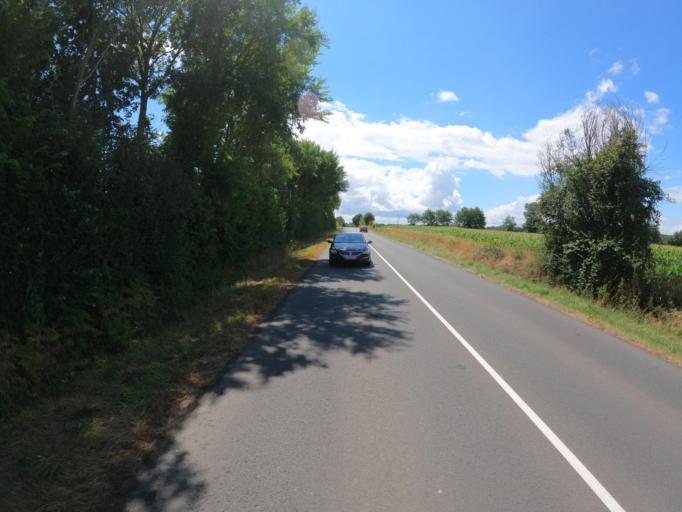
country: FR
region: Pays de la Loire
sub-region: Departement de Maine-et-Loire
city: Champigne
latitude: 47.6505
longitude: -0.5762
